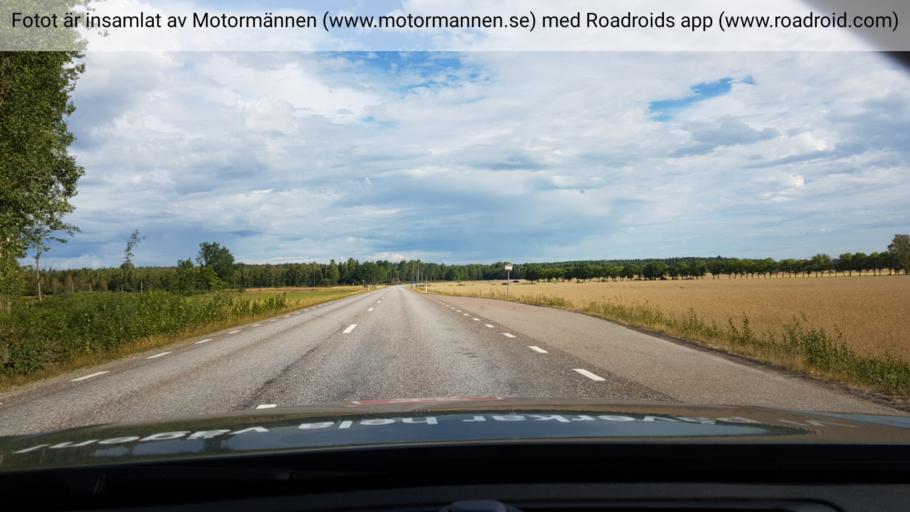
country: SE
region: Uppsala
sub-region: Enkopings Kommun
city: Irsta
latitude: 59.7927
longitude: 16.9016
